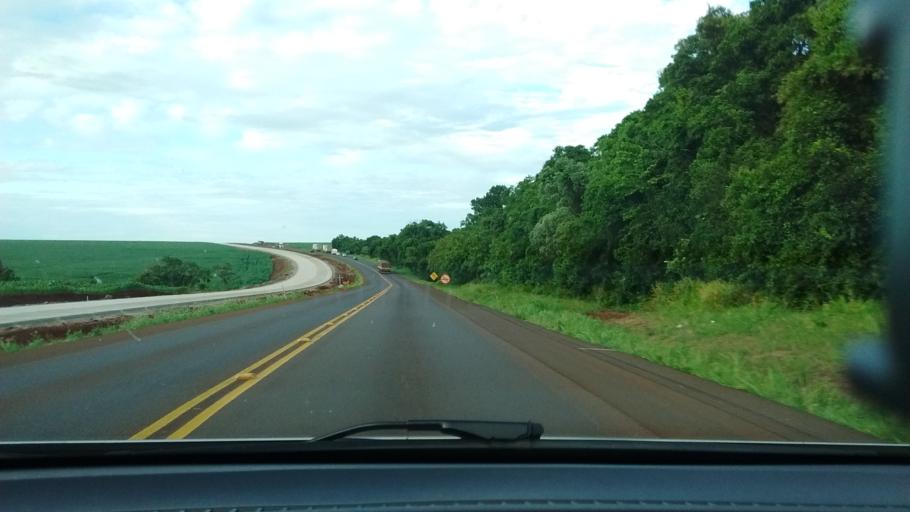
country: BR
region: Parana
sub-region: Cascavel
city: Cascavel
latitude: -25.0634
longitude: -53.5658
